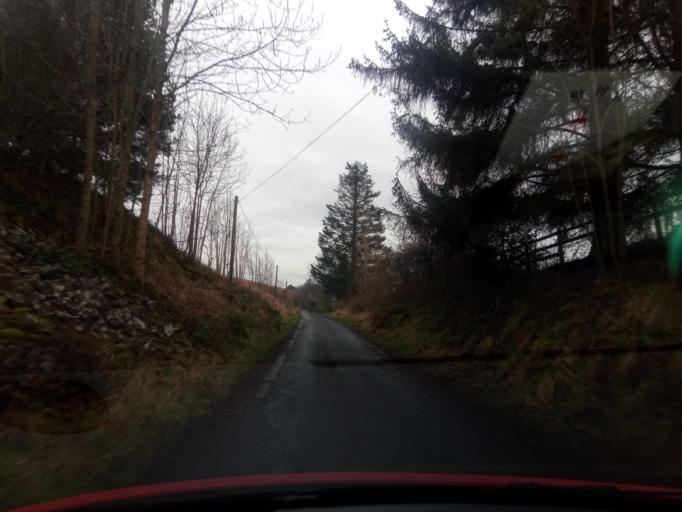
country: GB
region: England
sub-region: Northumberland
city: Rochester
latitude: 55.1807
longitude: -2.4332
